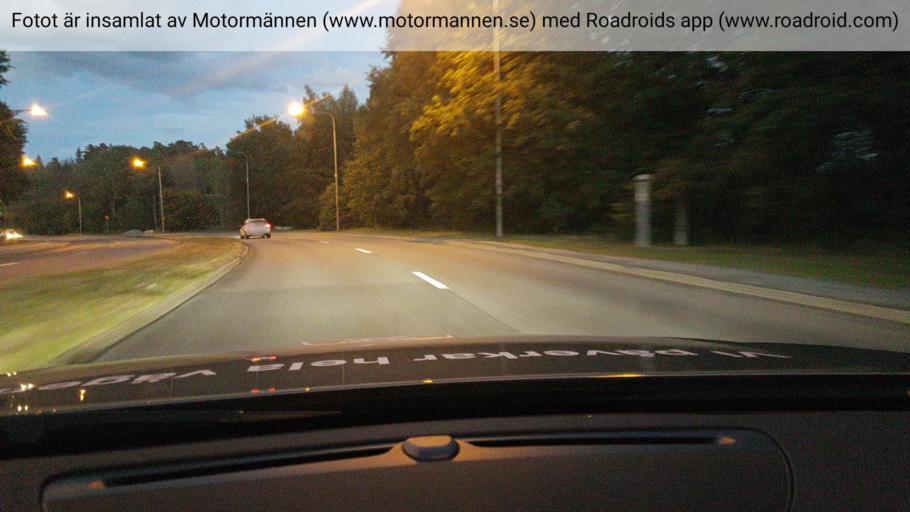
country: SE
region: Stockholm
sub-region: Stockholms Kommun
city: Arsta
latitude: 59.2599
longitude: 18.0374
